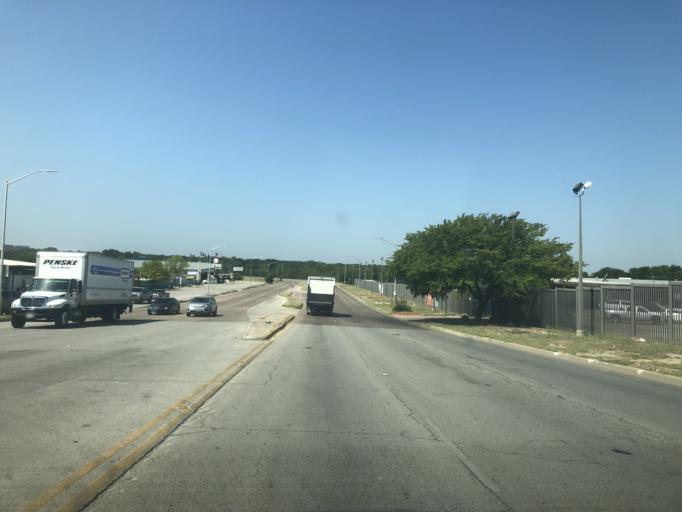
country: US
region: Texas
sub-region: Tarrant County
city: River Oaks
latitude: 32.7684
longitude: -97.3574
